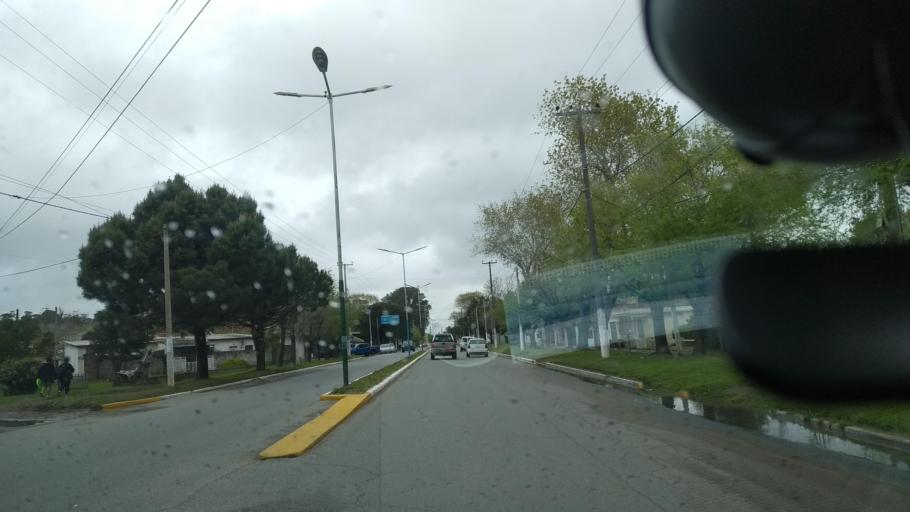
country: AR
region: Buenos Aires
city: San Clemente del Tuyu
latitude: -36.3751
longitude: -56.7188
